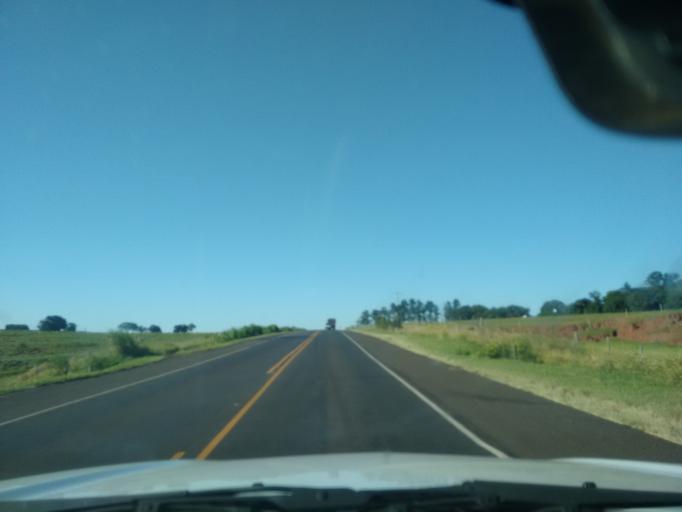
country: PY
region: Canindeyu
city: Salto del Guaira
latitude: -23.9765
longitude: -54.3309
